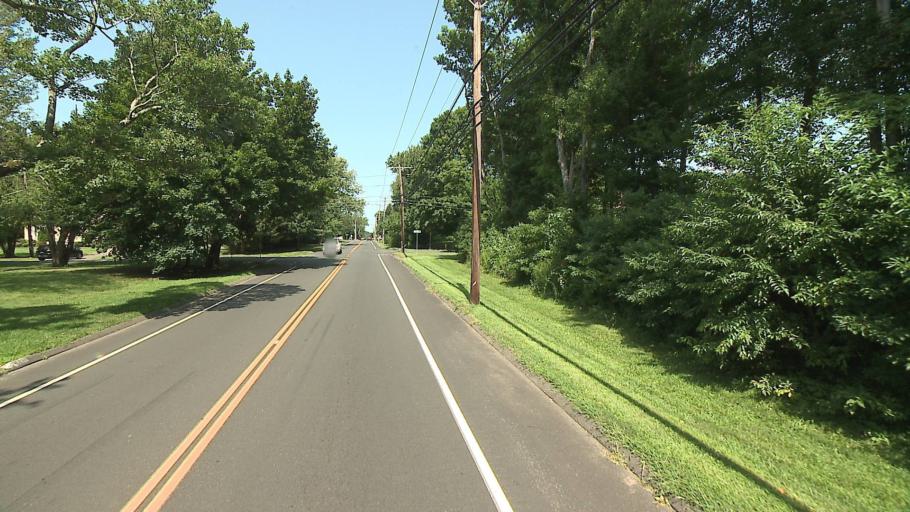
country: US
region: Connecticut
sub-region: Fairfield County
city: Trumbull
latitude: 41.2365
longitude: -73.2676
